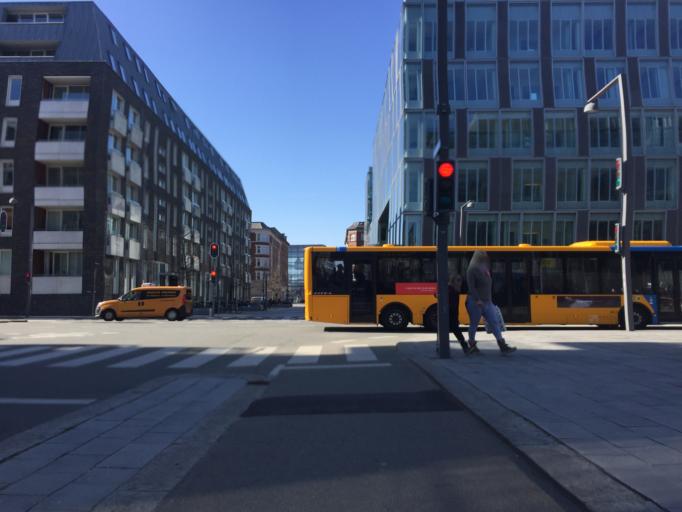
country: DK
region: Capital Region
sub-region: Kobenhavn
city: Christianshavn
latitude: 55.6676
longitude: 12.5817
